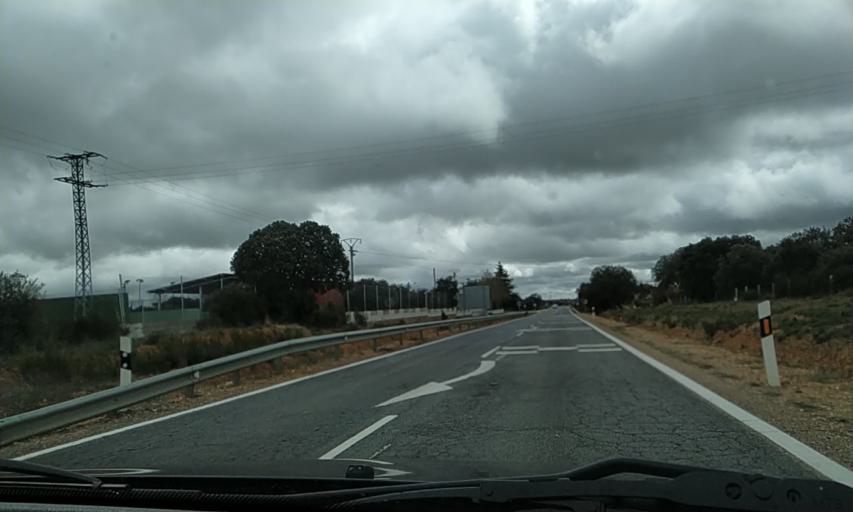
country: ES
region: Castille and Leon
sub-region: Provincia de Zamora
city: San Cebrian de Castro
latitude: 41.7115
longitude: -5.8082
